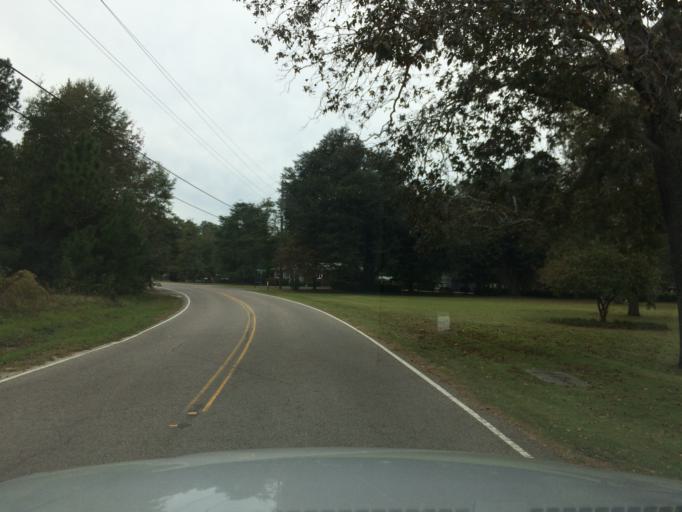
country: US
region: South Carolina
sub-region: Aiken County
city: New Ellenton
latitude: 33.4200
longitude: -81.6936
